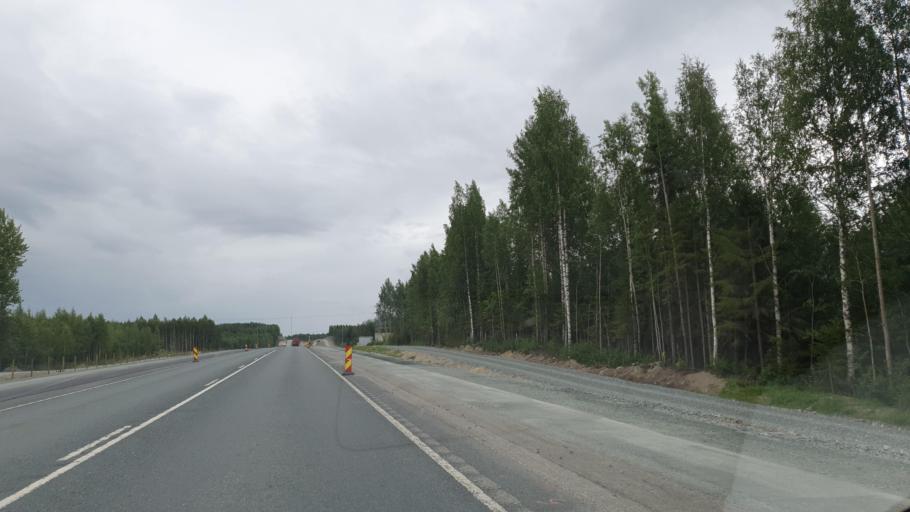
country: FI
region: Northern Savo
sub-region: Ylae-Savo
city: Lapinlahti
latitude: 63.2929
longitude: 27.4535
